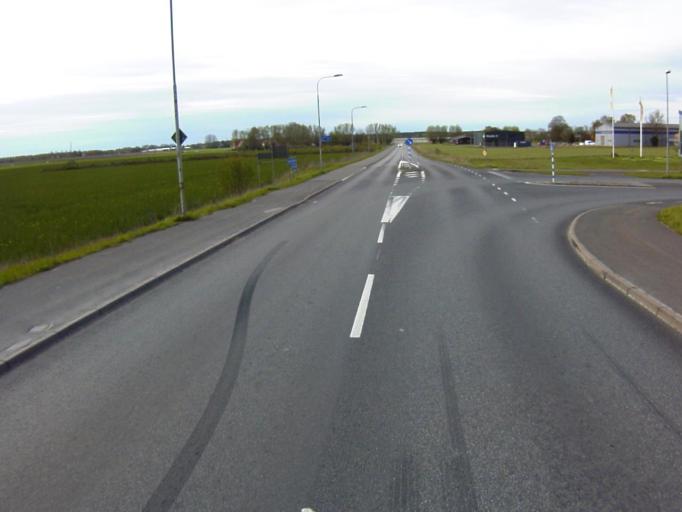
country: SE
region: Skane
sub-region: Kristianstads Kommun
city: Kristianstad
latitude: 56.0156
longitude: 14.1248
